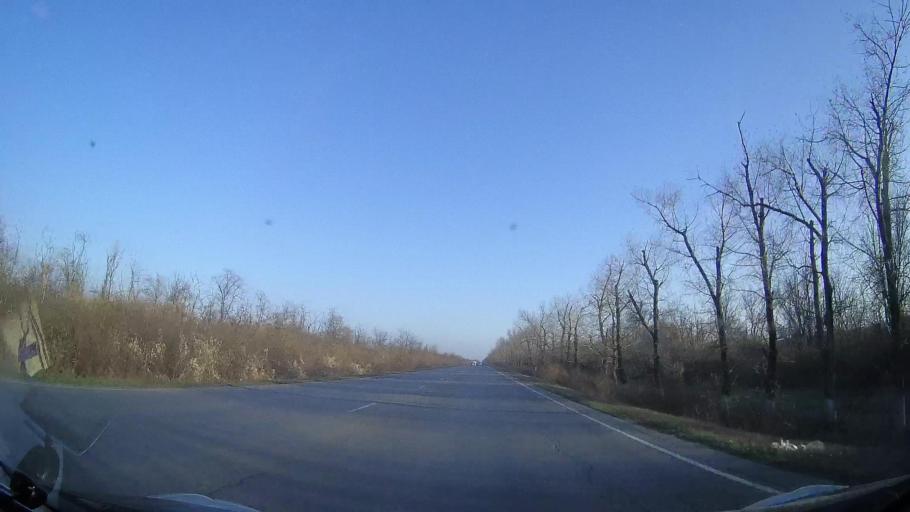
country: RU
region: Rostov
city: Bataysk
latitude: 47.0600
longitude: 39.8180
